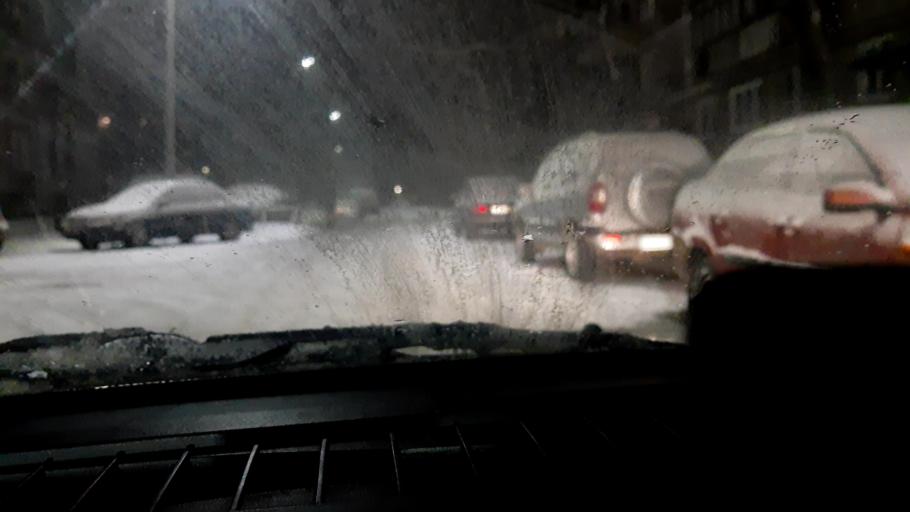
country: RU
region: Nizjnij Novgorod
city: Kstovo
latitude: 56.1475
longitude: 44.1818
